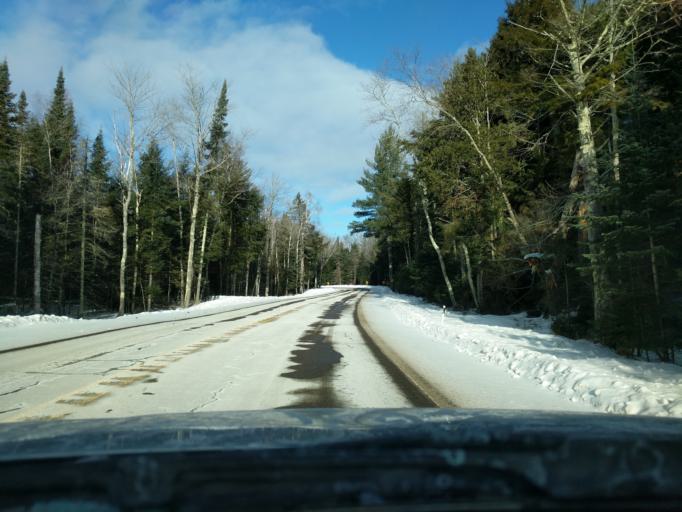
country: US
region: Wisconsin
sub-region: Vilas County
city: Eagle River
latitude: 45.7682
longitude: -89.0673
